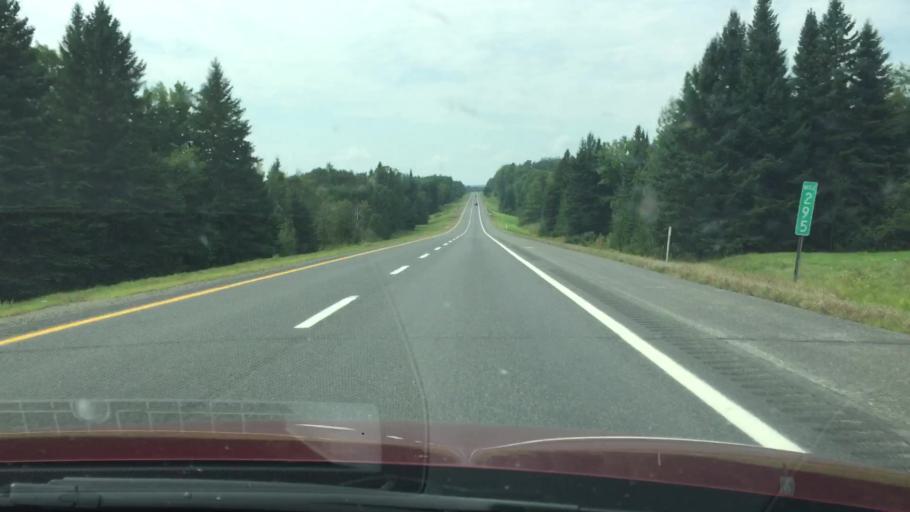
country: US
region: Maine
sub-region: Aroostook County
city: Houlton
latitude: 46.1411
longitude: -67.9812
